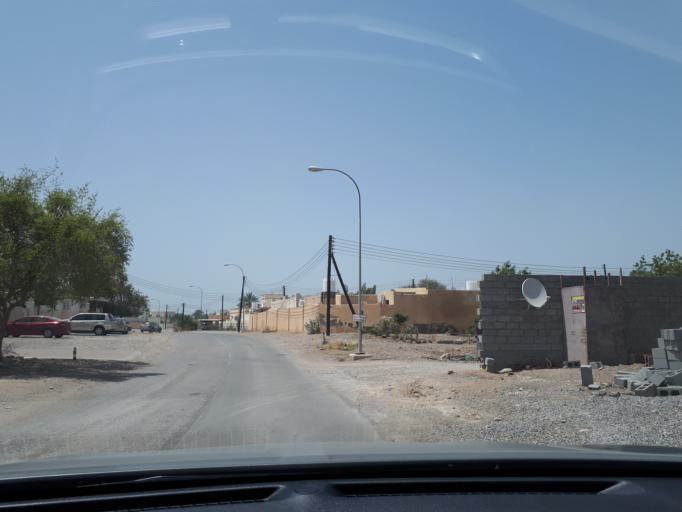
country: OM
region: Muhafazat Masqat
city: As Sib al Jadidah
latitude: 23.6865
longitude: 58.1154
